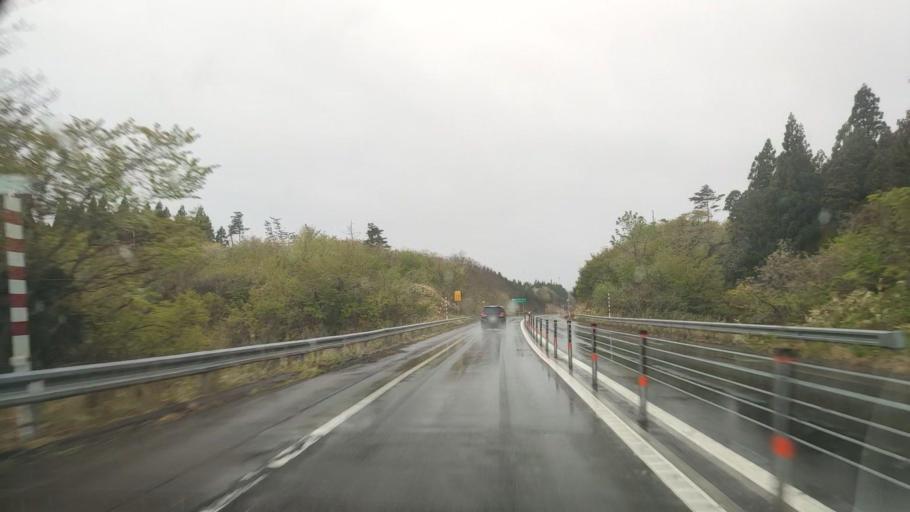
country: JP
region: Akita
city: Noshiromachi
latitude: 40.1644
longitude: 140.0464
